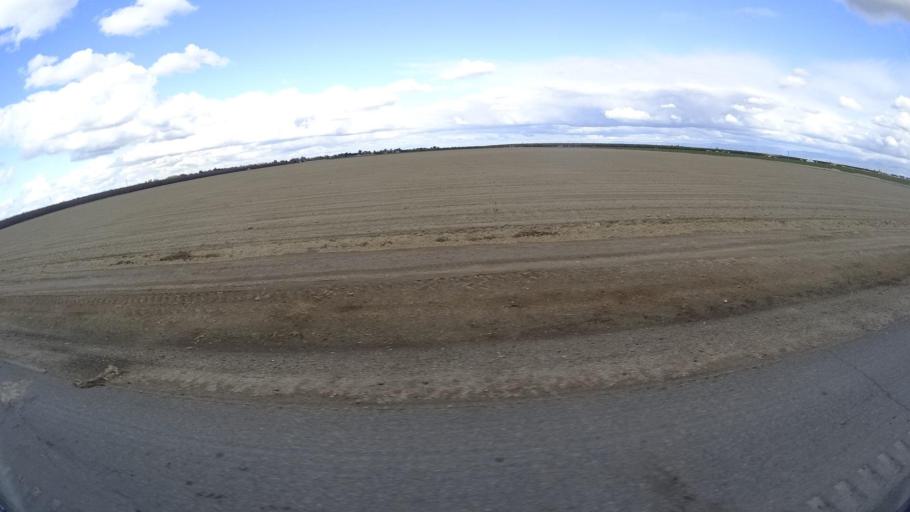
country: US
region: California
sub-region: Kern County
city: Greenfield
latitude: 35.2088
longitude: -119.0713
